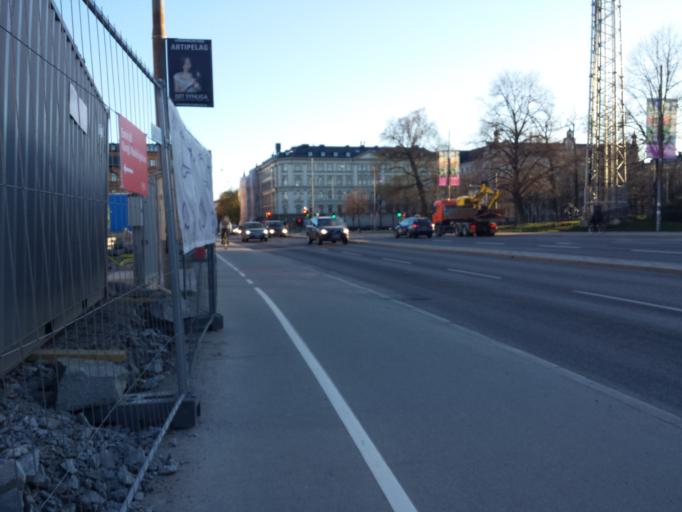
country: SE
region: Stockholm
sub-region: Stockholms Kommun
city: OEstermalm
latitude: 59.3447
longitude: 18.0801
